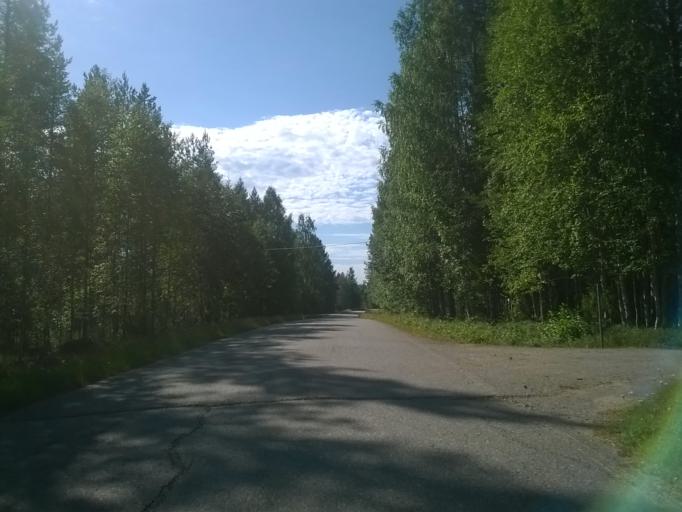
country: FI
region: Kainuu
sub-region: Kehys-Kainuu
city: Kuhmo
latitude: 64.1345
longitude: 29.4066
